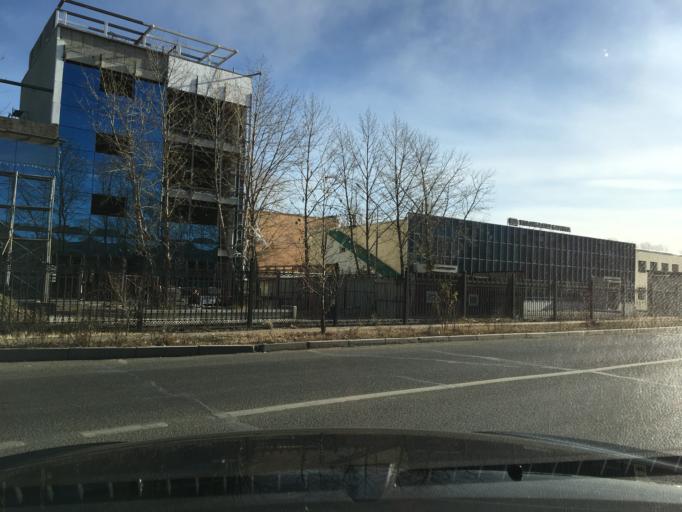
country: MN
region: Ulaanbaatar
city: Ulaanbaatar
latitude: 47.8954
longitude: 106.8734
